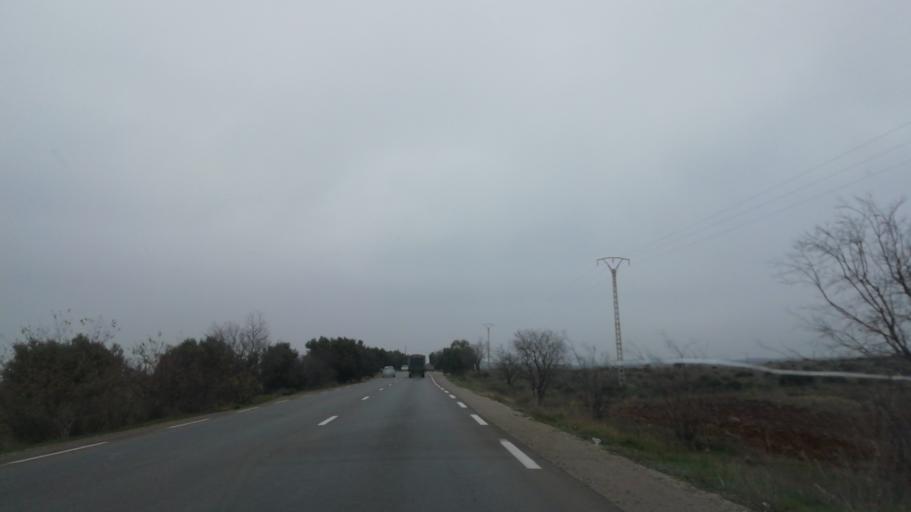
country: DZ
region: Mascara
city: Mascara
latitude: 35.3147
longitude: 0.3824
